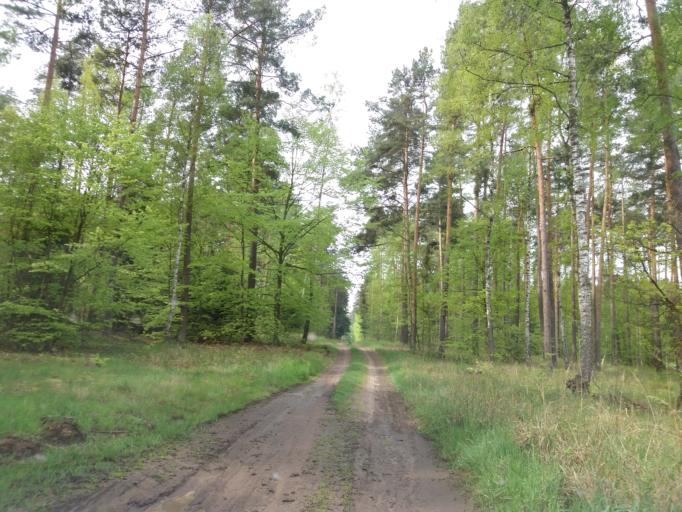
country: PL
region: West Pomeranian Voivodeship
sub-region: Powiat choszczenski
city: Krzecin
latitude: 53.0152
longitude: 15.5481
